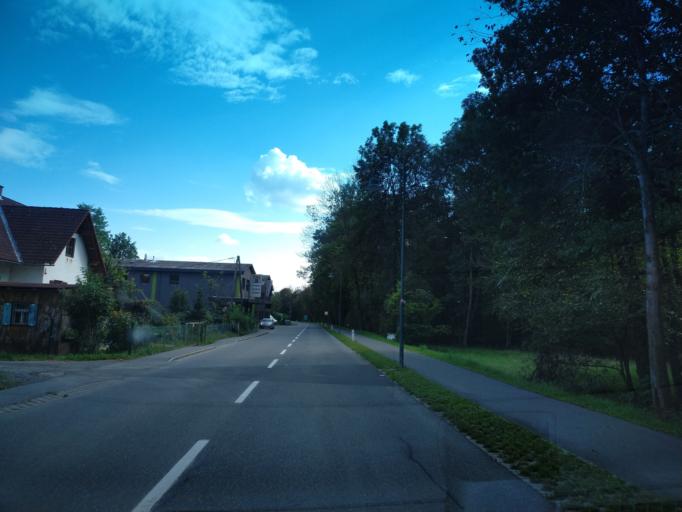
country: AT
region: Styria
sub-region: Politischer Bezirk Leibnitz
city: Kaindorf an der Sulm
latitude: 46.7874
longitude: 15.5339
